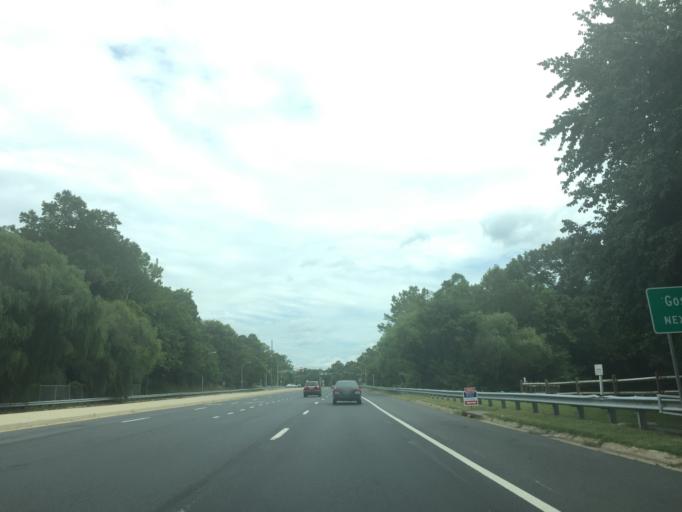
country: US
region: Maryland
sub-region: Montgomery County
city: Gaithersburg
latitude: 39.1584
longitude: -77.1949
